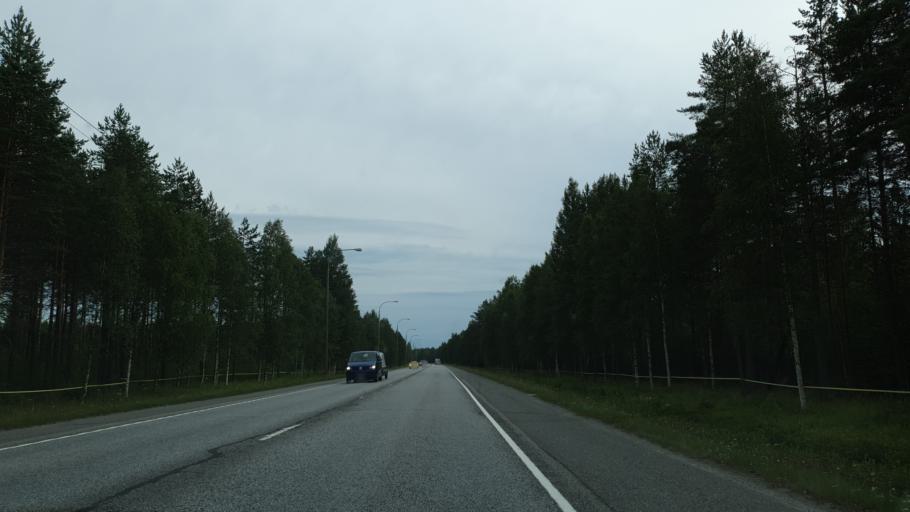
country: FI
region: North Karelia
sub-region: Joensuu
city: Joensuu
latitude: 62.6598
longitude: 29.7860
